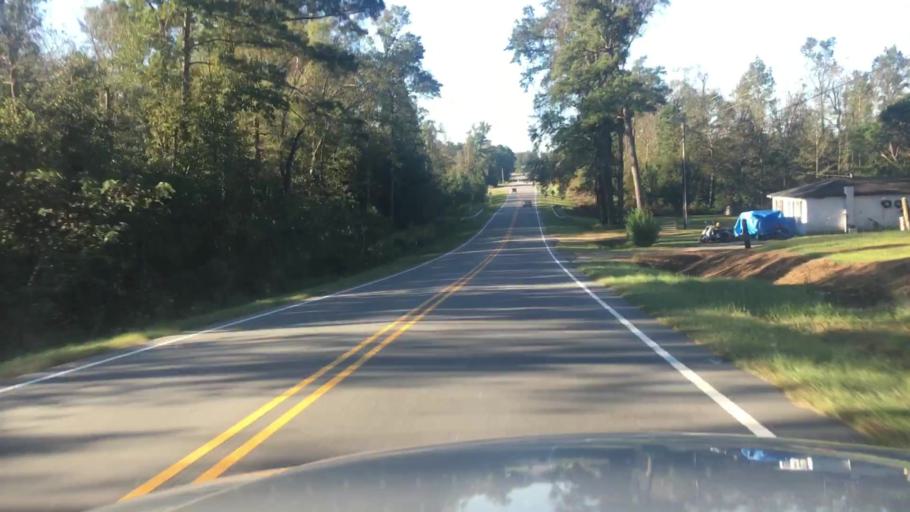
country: US
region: North Carolina
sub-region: Cumberland County
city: Spring Lake
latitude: 35.2598
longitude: -78.9234
